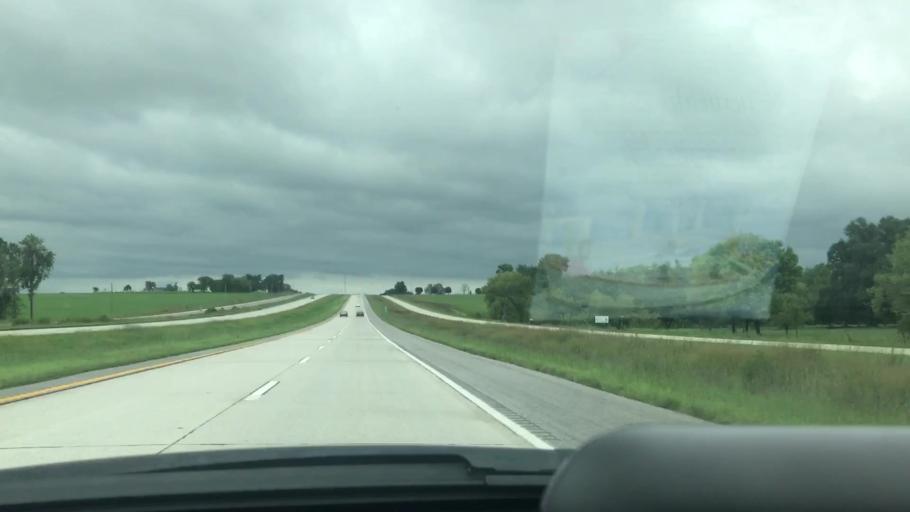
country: US
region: Missouri
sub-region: Greene County
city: Fair Grove
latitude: 37.4295
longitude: -93.1448
